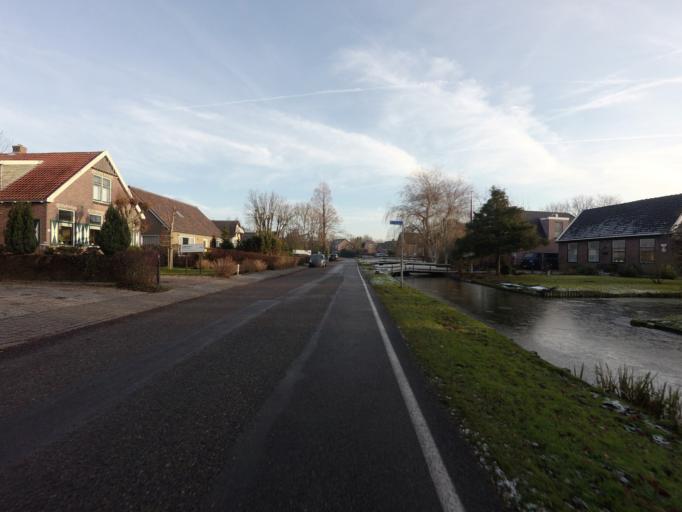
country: NL
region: Utrecht
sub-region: Gemeente De Ronde Venen
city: Mijdrecht
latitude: 52.1947
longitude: 4.8926
